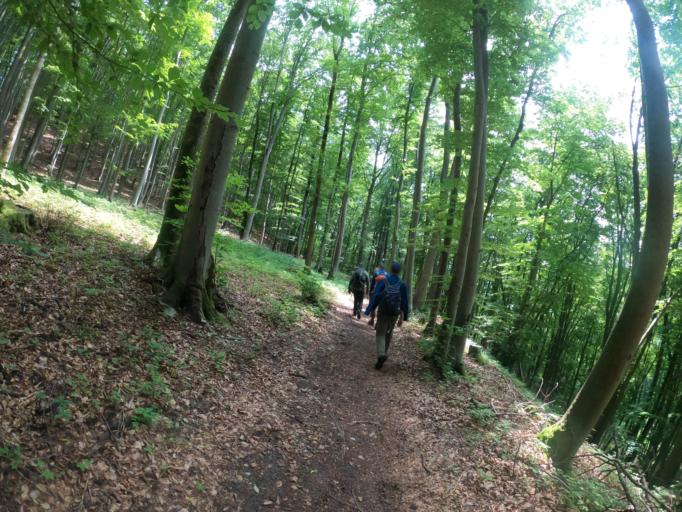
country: DE
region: Bavaria
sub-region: Upper Franconia
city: Litzendorf
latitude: 49.9251
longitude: 11.0575
